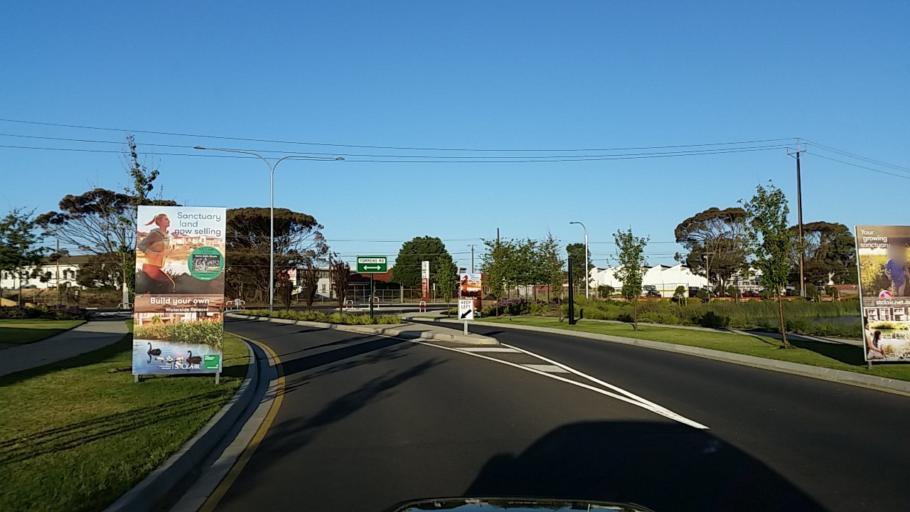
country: AU
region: South Australia
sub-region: Charles Sturt
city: Woodville North
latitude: -34.8678
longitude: 138.5346
